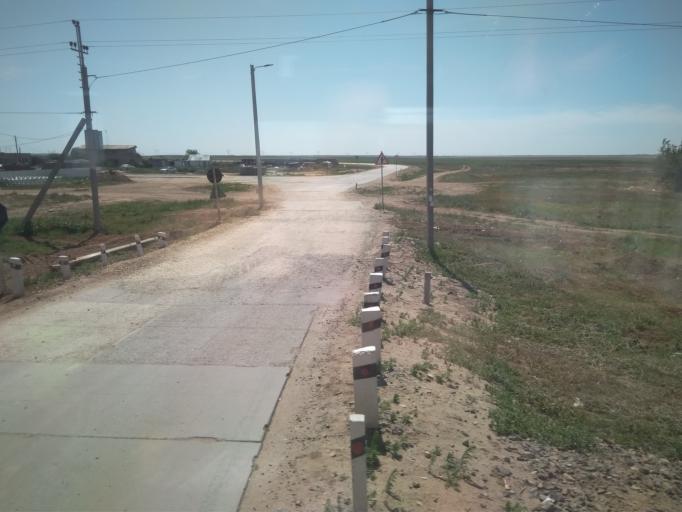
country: RU
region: Volgograd
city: Bereslavka
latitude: 48.2842
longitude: 44.2691
